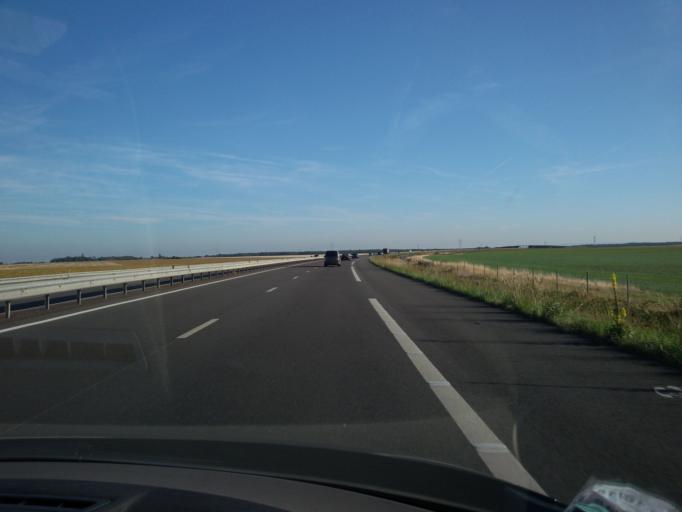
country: FR
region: Centre
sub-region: Departement du Cher
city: Levet
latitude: 46.9487
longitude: 2.4165
